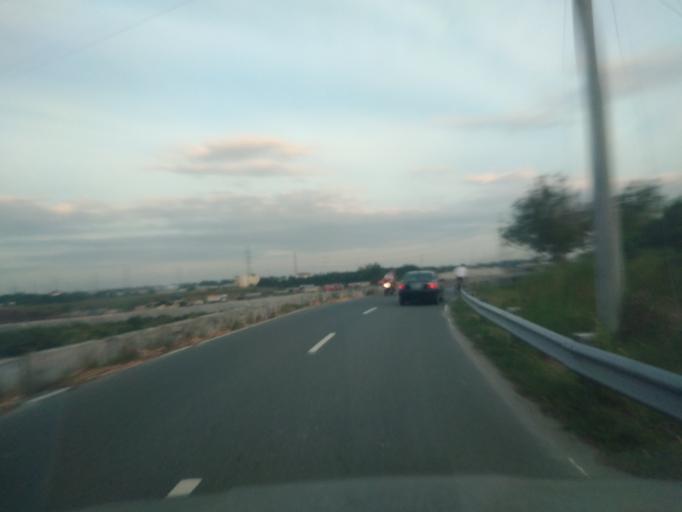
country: PH
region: Central Luzon
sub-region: Province of Pampanga
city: Bacolor
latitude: 15.0002
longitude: 120.6359
